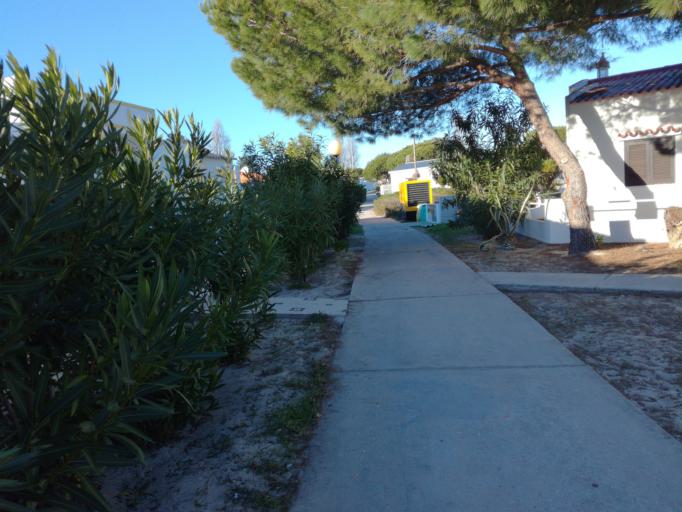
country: PT
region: Faro
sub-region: Olhao
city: Olhao
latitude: 37.0178
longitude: -7.8023
